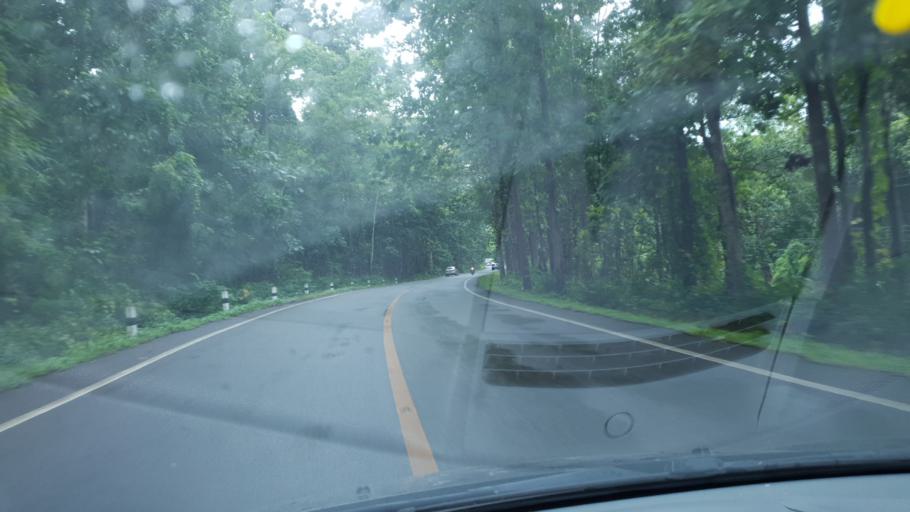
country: TH
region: Mae Hong Son
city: Pa Pae
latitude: 18.2378
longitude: 97.9445
